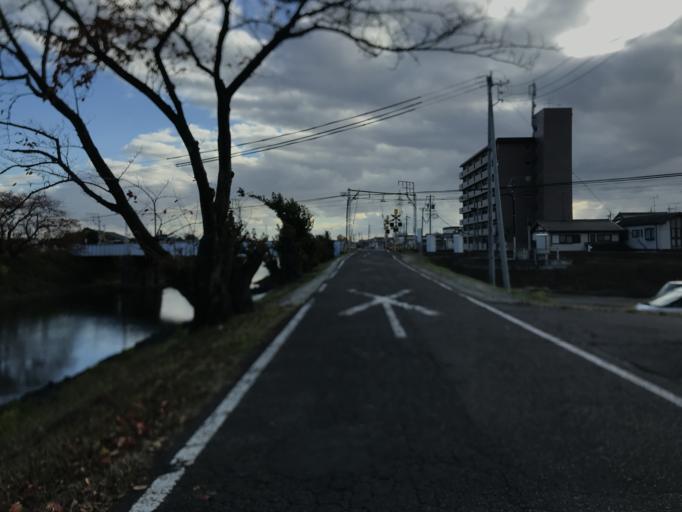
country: JP
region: Aichi
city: Inazawa
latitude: 35.2098
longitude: 136.8379
